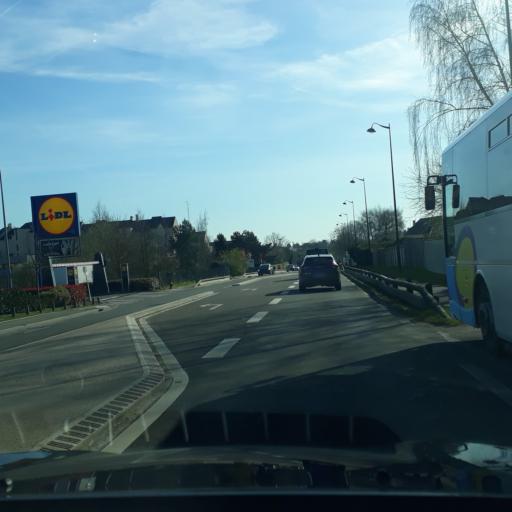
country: FR
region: Ile-de-France
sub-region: Departement de l'Essonne
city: Etampes
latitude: 48.4408
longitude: 2.1461
